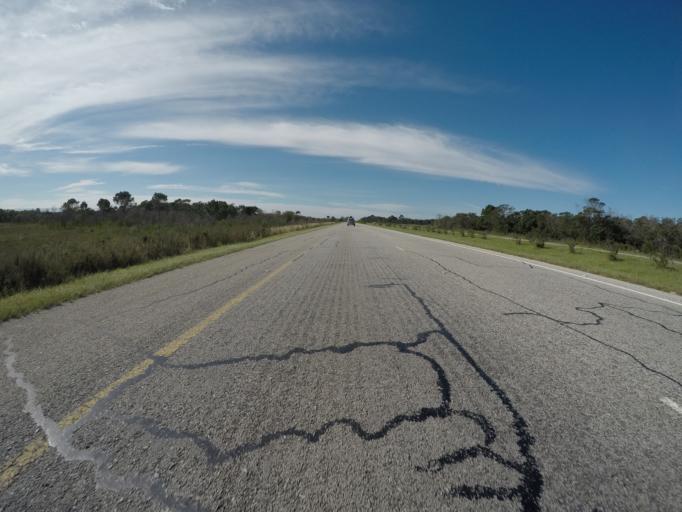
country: ZA
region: Eastern Cape
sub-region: Nelson Mandela Bay Metropolitan Municipality
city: Uitenhage
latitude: -33.9327
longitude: 25.3528
